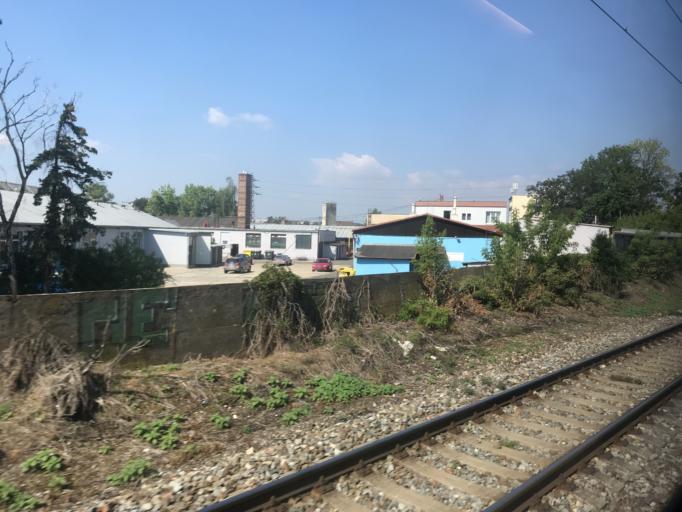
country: CZ
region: Praha
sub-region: Praha 9
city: Vysocany
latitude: 50.0646
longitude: 14.4984
